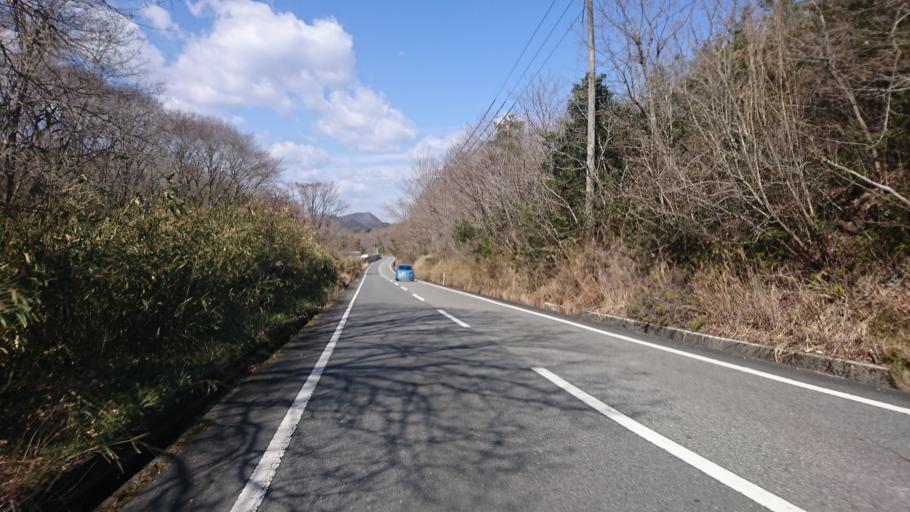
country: JP
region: Hyogo
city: Kakogawacho-honmachi
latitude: 34.8580
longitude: 134.8037
